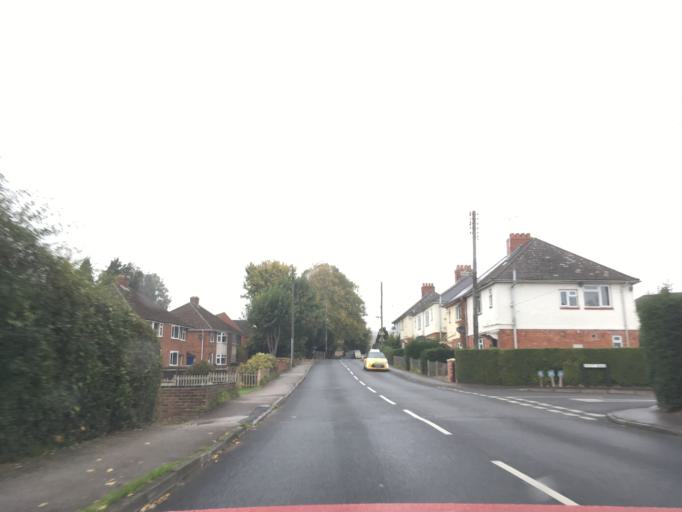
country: GB
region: England
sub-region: Gloucestershire
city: Stonehouse
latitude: 51.7455
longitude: -2.2440
